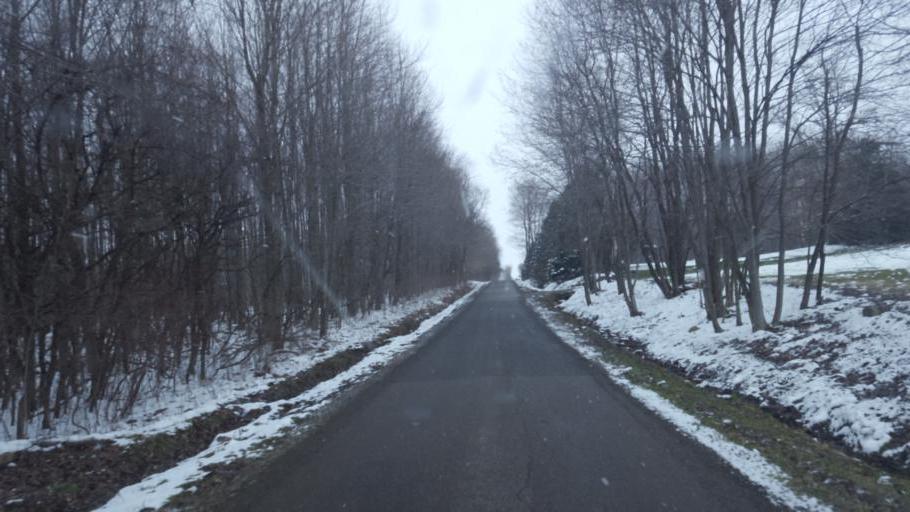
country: US
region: Pennsylvania
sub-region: Mercer County
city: Stoneboro
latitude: 41.4269
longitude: -80.0925
